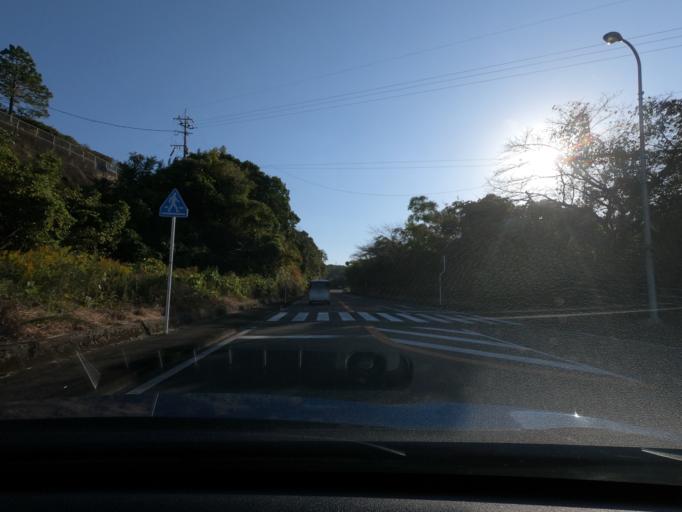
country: JP
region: Kagoshima
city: Akune
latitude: 32.0576
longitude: 130.2220
